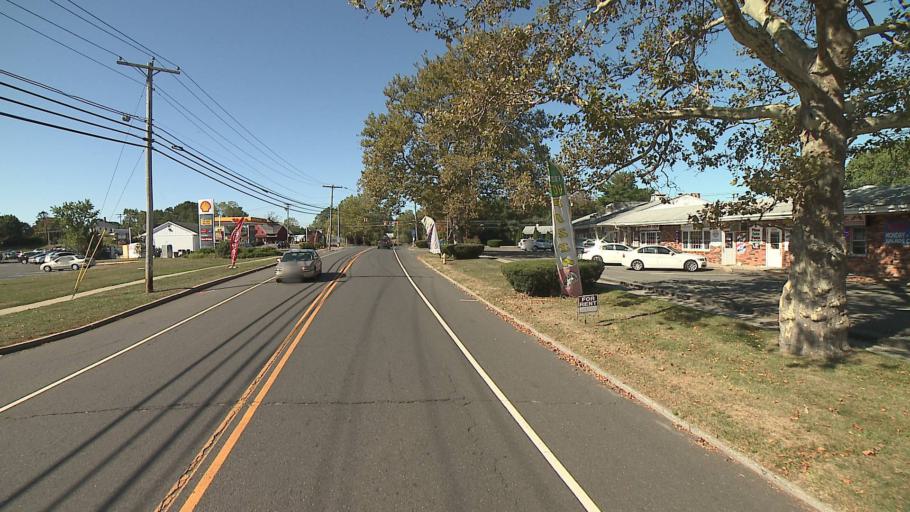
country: US
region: Connecticut
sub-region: New Haven County
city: Woodmont
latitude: 41.2288
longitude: -72.9961
